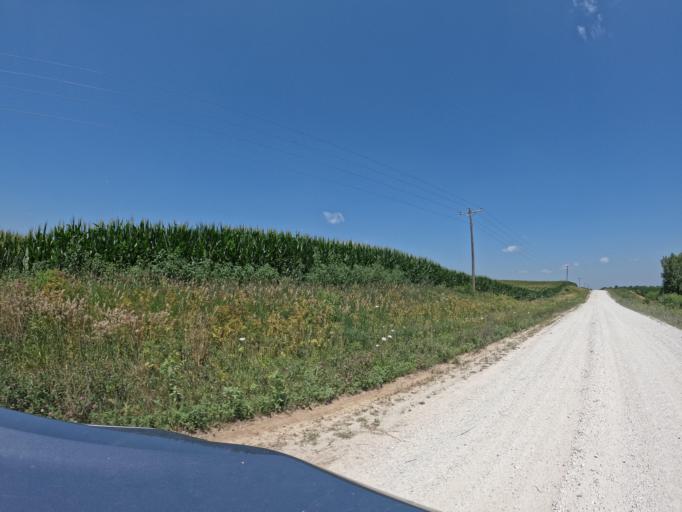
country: US
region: Iowa
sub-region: Keokuk County
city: Sigourney
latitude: 41.2729
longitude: -92.2382
